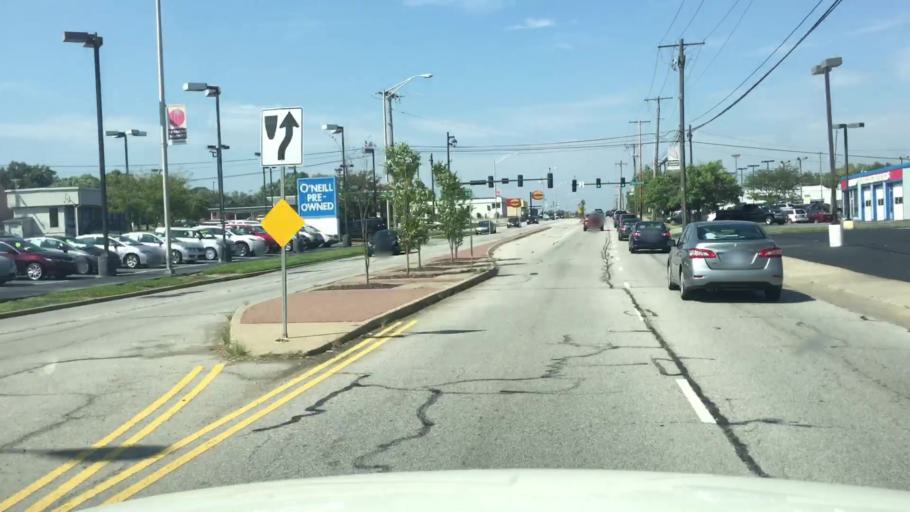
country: US
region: Kansas
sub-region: Johnson County
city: Overland Park
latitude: 38.9848
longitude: -94.6677
